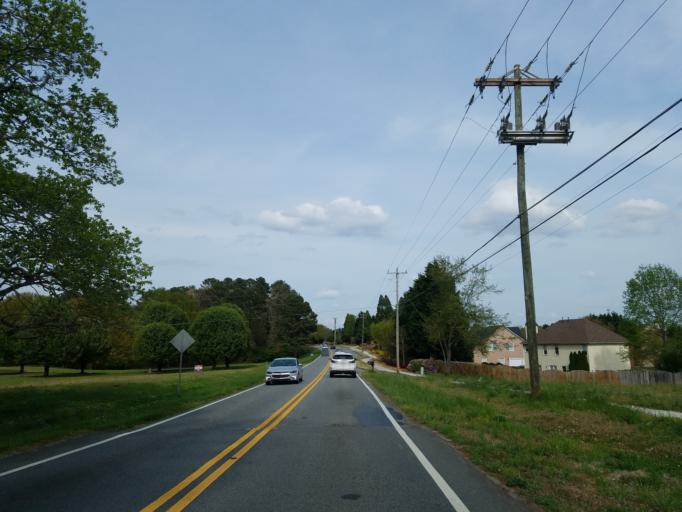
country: US
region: Georgia
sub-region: Fulton County
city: Johns Creek
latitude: 34.1098
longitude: -84.1880
